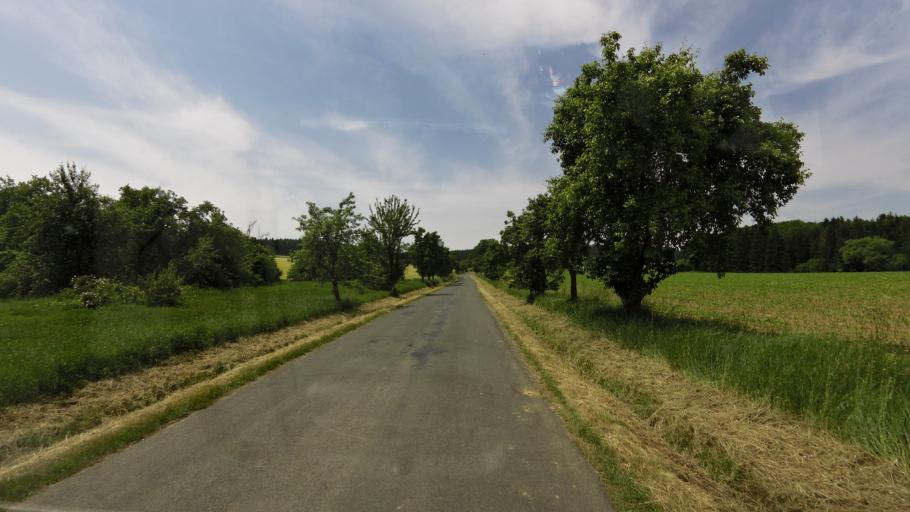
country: CZ
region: Plzensky
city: St'ahlavy
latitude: 49.6745
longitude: 13.4884
